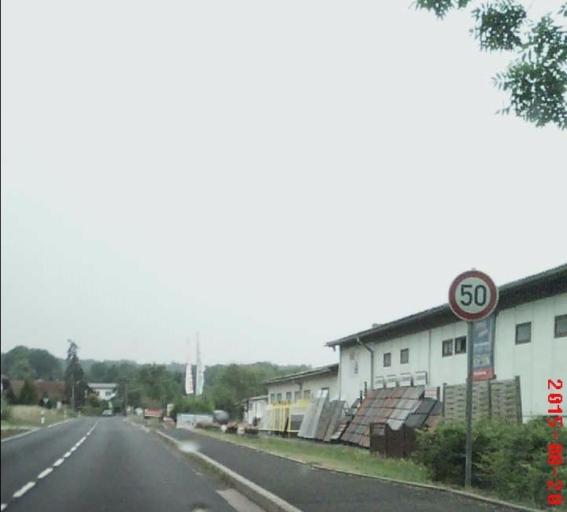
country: DE
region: Thuringia
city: Hellingen
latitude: 50.2833
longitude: 10.7270
